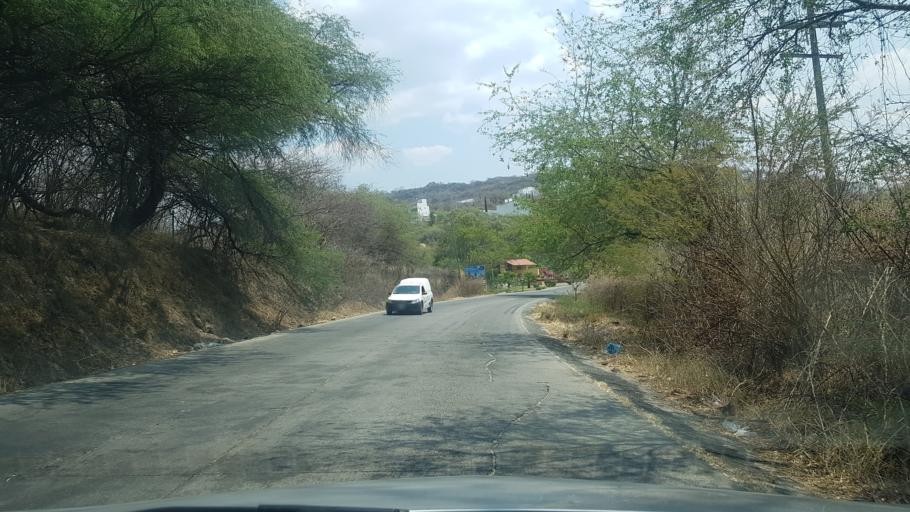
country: MX
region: Morelos
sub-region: Tlaltizapan de Zapata
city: Colonia Palo Prieto (Chipitongo)
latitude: 18.7467
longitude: -99.1122
